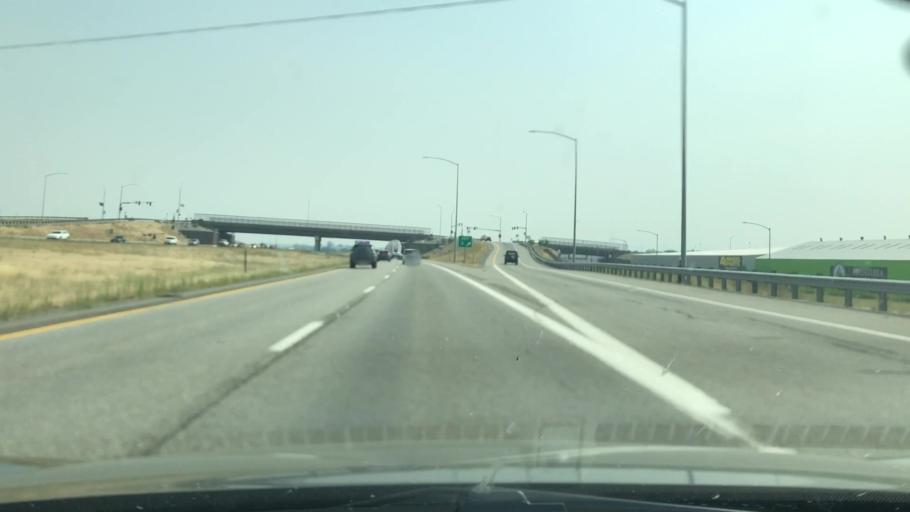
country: US
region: Washington
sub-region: Spokane County
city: Otis Orchards-East Farms
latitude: 47.7000
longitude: -117.0233
